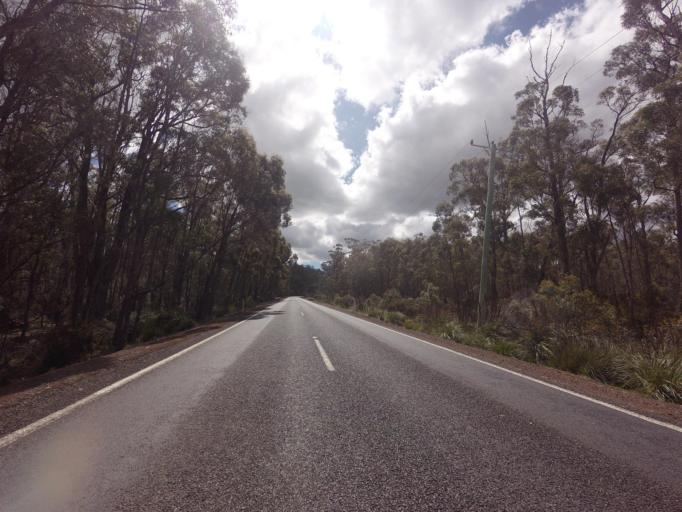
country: AU
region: Tasmania
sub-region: Northern Midlands
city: Evandale
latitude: -42.0178
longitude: 147.7382
